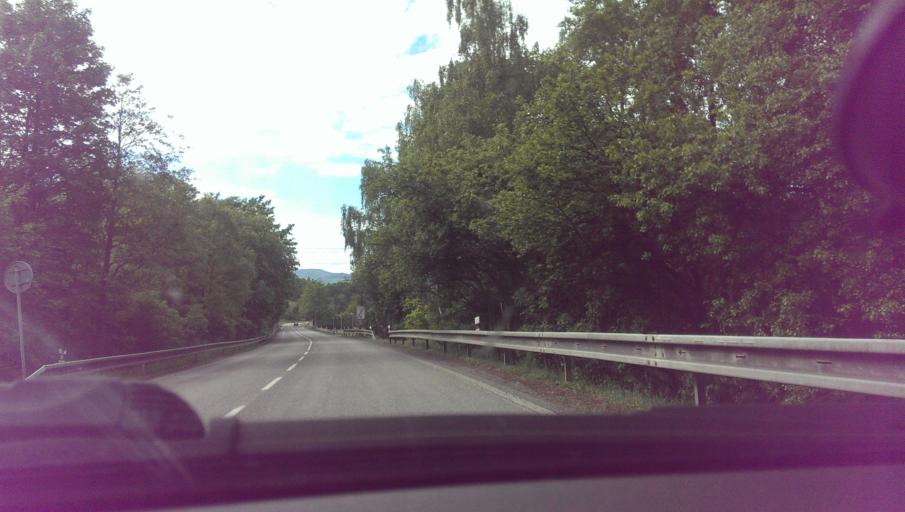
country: CZ
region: Zlin
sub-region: Okres Vsetin
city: Roznov pod Radhostem
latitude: 49.4877
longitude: 18.1700
